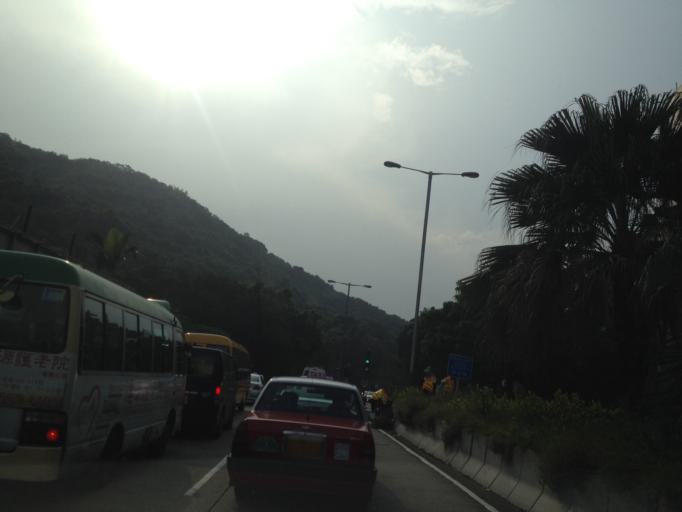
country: HK
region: Wanchai
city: Wan Chai
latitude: 22.2737
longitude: 114.2314
